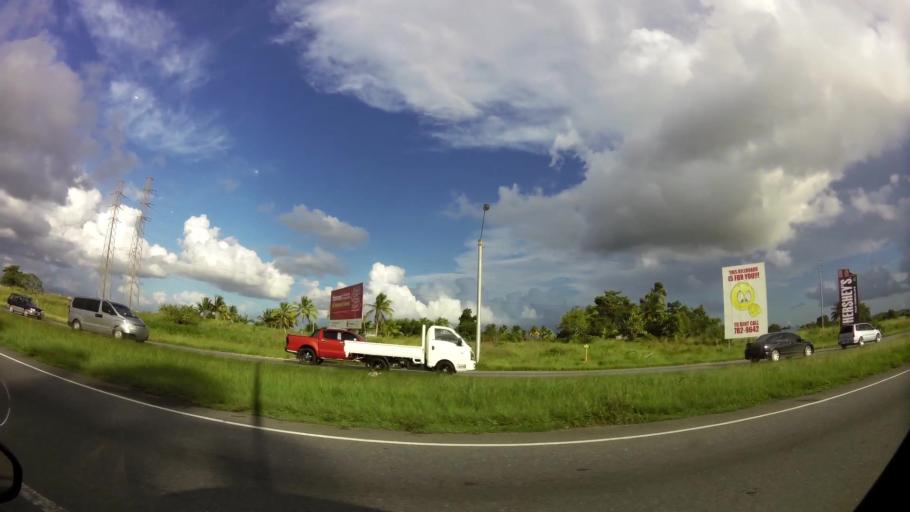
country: TT
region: Chaguanas
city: Chaguanas
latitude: 10.5007
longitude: -61.4069
